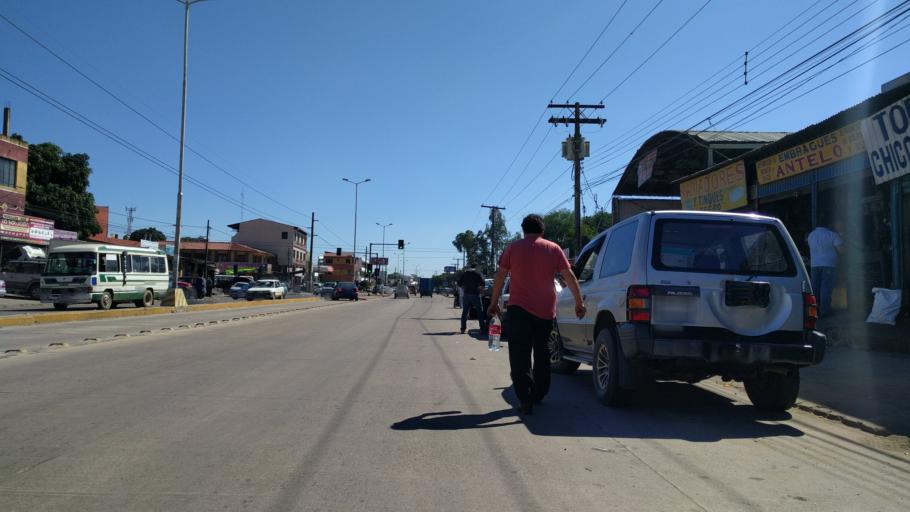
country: BO
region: Santa Cruz
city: Santa Cruz de la Sierra
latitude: -17.8071
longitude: -63.1965
